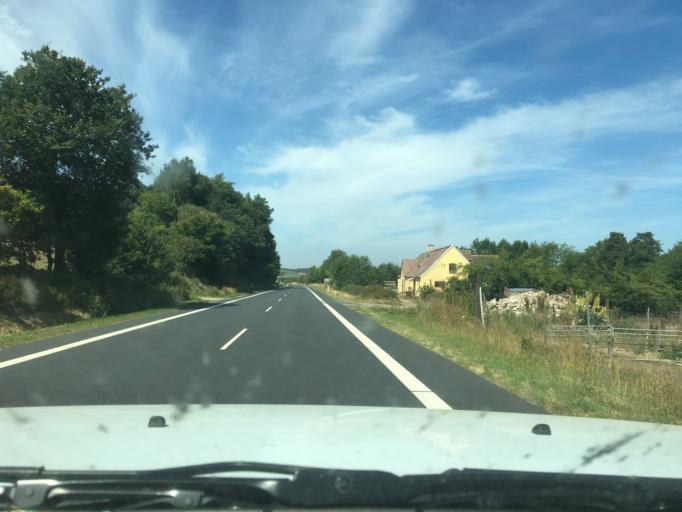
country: DK
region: Central Jutland
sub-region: Viborg Kommune
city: Viborg
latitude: 56.5239
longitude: 9.4045
